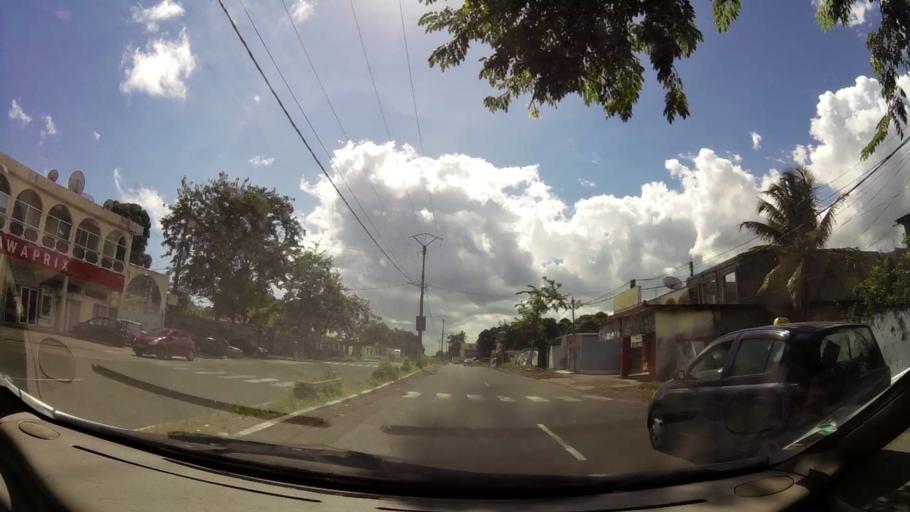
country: KM
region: Grande Comore
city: Mavingouni
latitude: -11.7150
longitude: 43.2459
